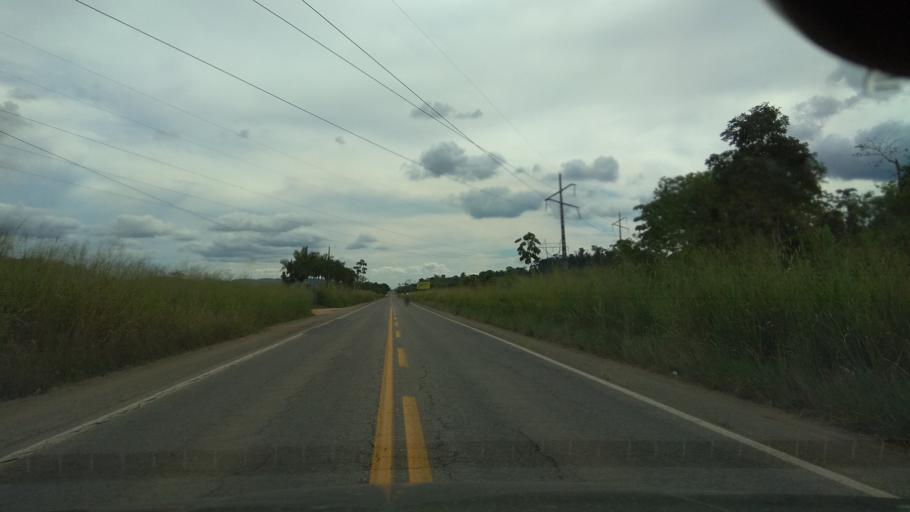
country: BR
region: Bahia
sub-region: Ipiau
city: Ipiau
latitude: -14.1473
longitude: -39.7046
